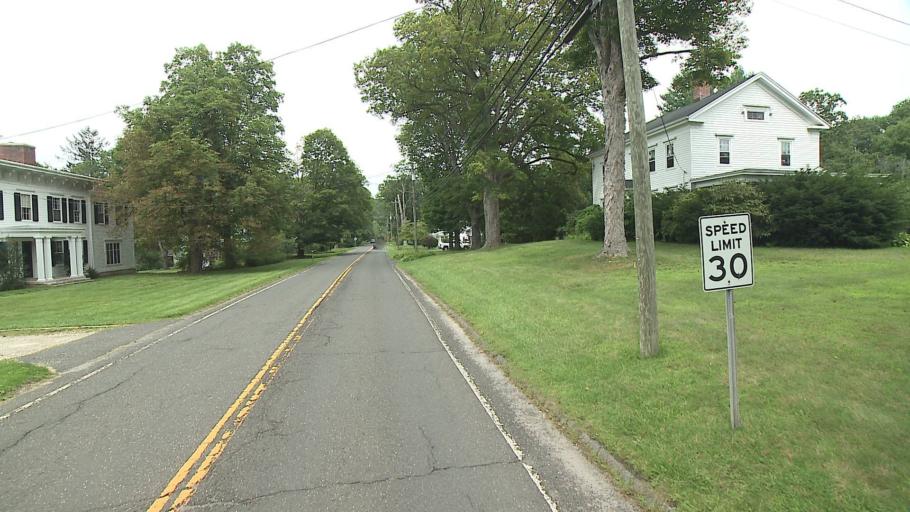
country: US
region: Connecticut
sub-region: Litchfield County
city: New Milford
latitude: 41.5356
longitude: -73.3666
